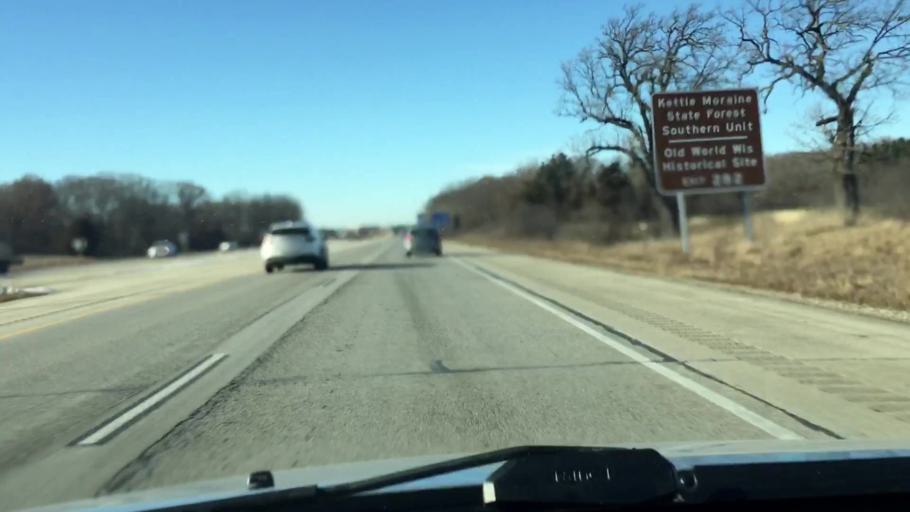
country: US
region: Wisconsin
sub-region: Waukesha County
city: Delafield
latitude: 43.0650
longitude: -88.4558
